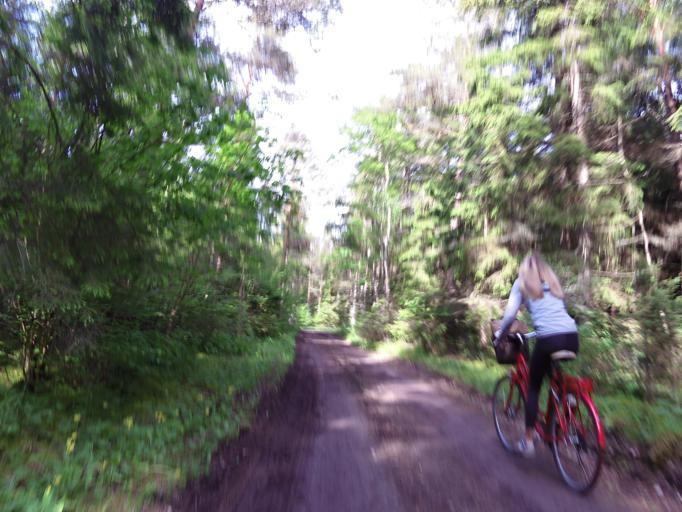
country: EE
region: Harju
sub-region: Paldiski linn
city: Paldiski
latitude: 59.2670
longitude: 23.7515
